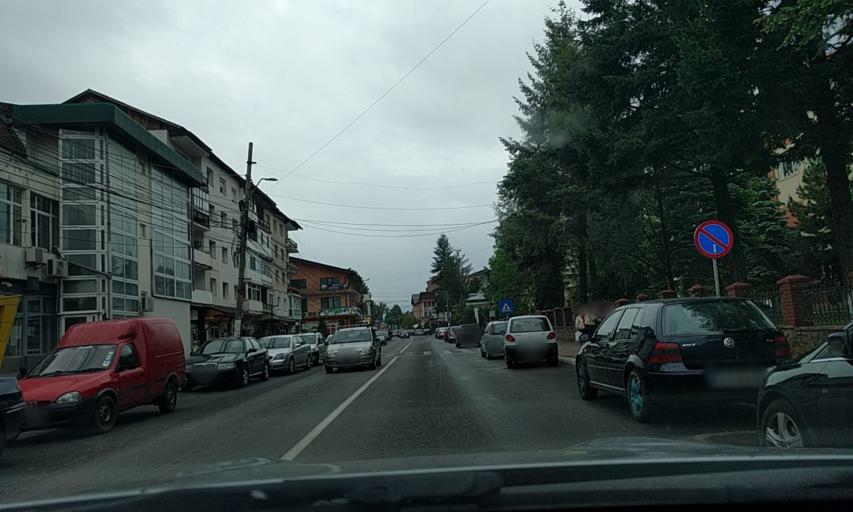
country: RO
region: Dambovita
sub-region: Oras Pucioasa
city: Pucioasa
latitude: 45.0749
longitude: 25.4349
